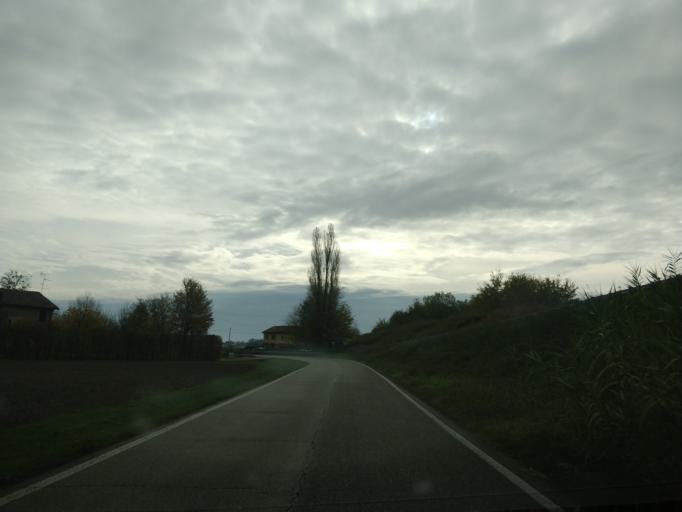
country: IT
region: Emilia-Romagna
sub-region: Provincia di Bologna
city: Argelato
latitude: 44.6200
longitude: 11.3165
